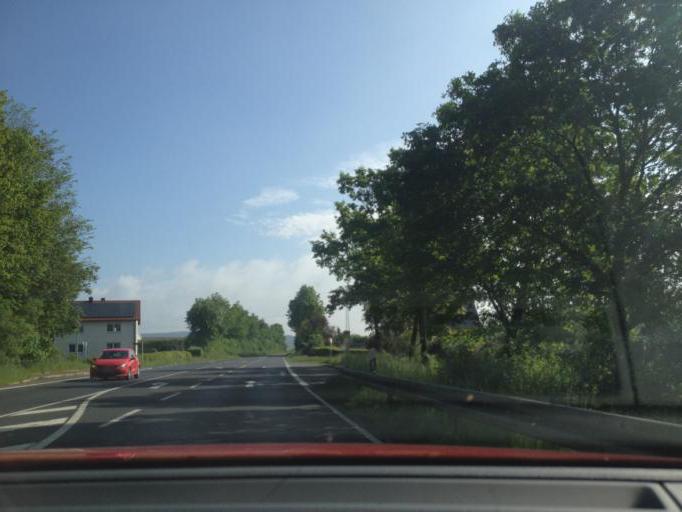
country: DE
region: Bavaria
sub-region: Upper Palatinate
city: Kemnath
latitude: 49.8854
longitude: 11.8890
